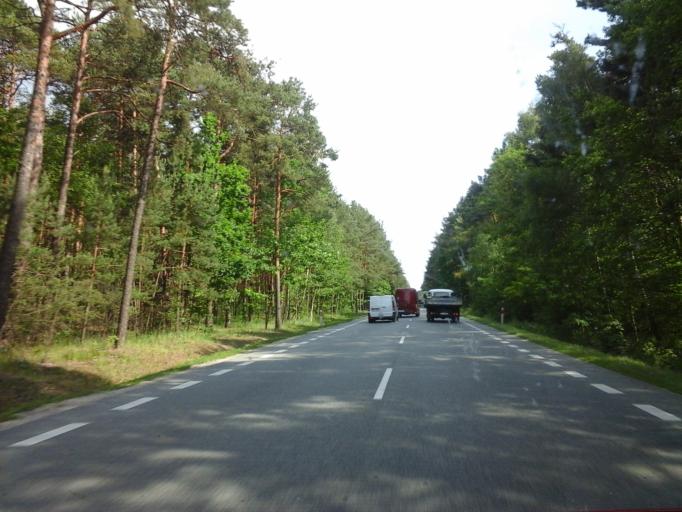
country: PL
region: Swietokrzyskie
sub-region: Powiat konecki
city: Ruda Maleniecka
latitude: 51.1601
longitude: 20.2294
